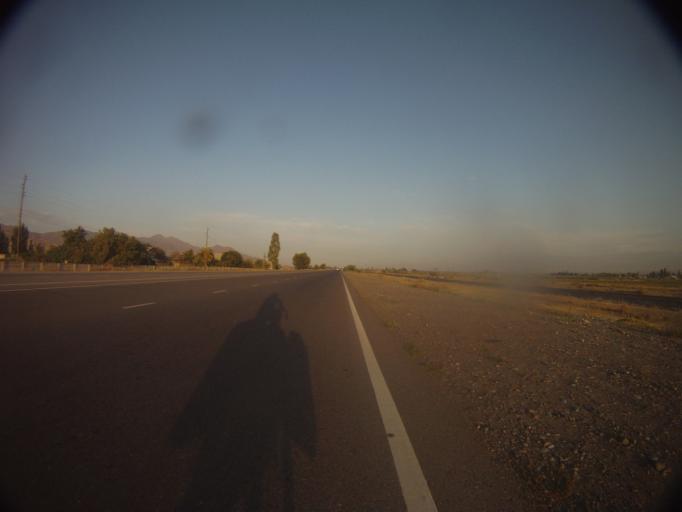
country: KG
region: Chuy
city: Tokmok
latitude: 42.8483
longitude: 75.3386
